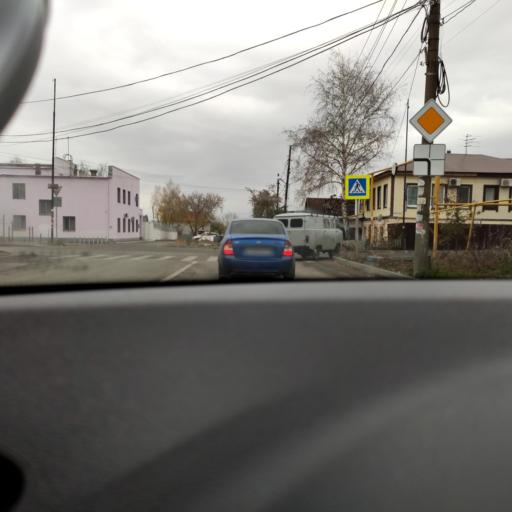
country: RU
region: Samara
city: Samara
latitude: 53.1808
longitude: 50.1344
